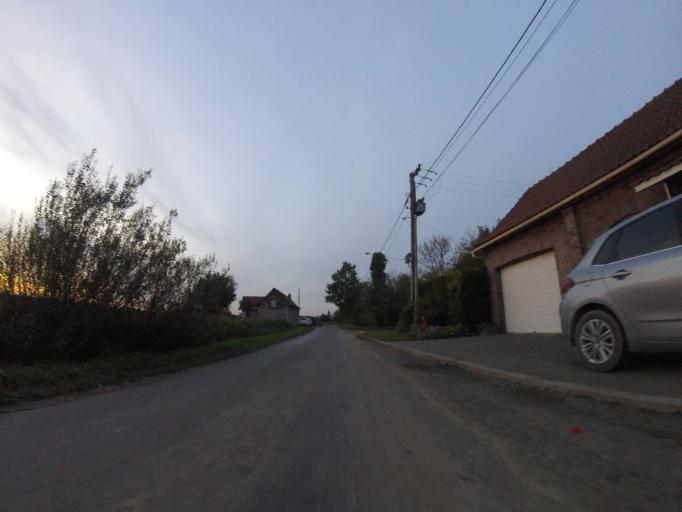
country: FR
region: Nord-Pas-de-Calais
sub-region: Departement du Pas-de-Calais
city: Sailly-sur-la-Lys
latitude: 50.6464
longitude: 2.7700
